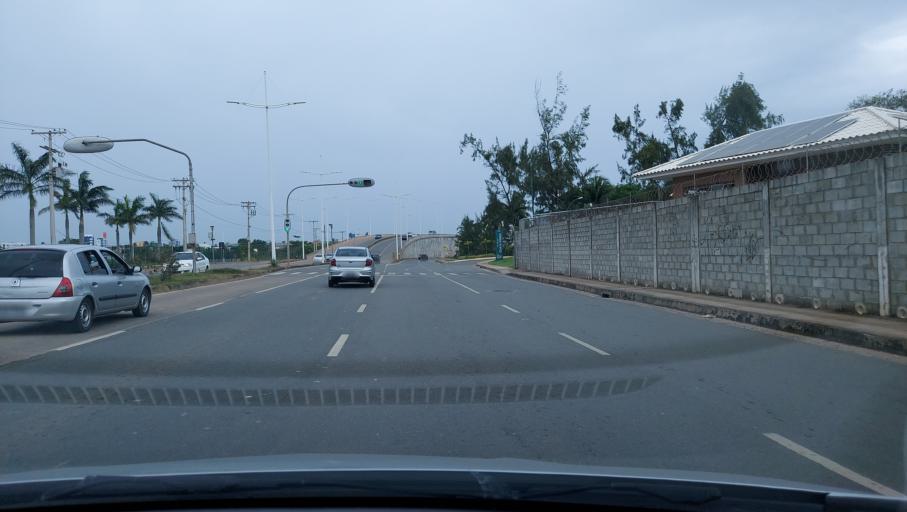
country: BR
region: Bahia
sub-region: Lauro De Freitas
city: Lauro de Freitas
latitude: -12.9454
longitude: -38.3849
